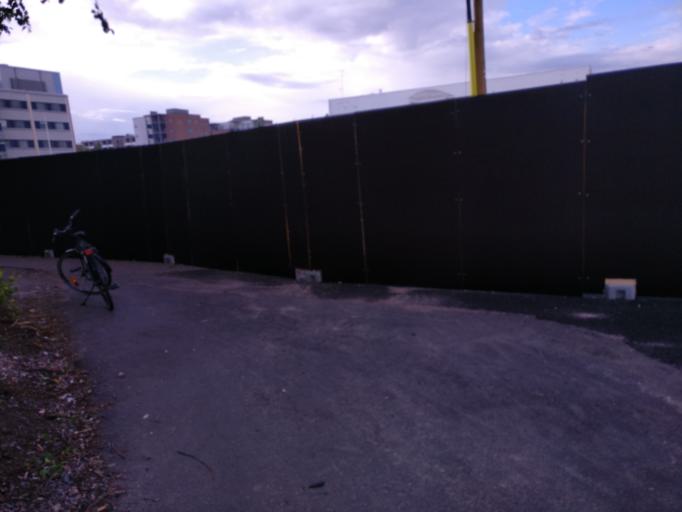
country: FI
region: Uusimaa
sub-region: Helsinki
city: Teekkarikylae
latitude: 60.2618
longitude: 24.8510
